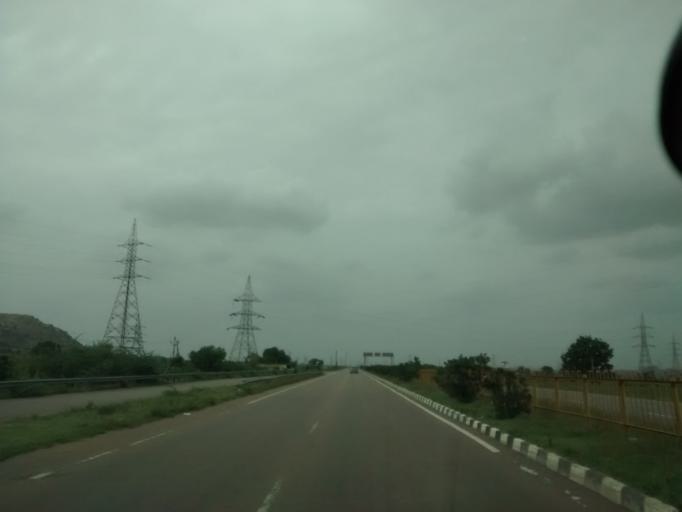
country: IN
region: Andhra Pradesh
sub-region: Kurnool
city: Ramapuram
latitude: 15.1149
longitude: 77.6608
